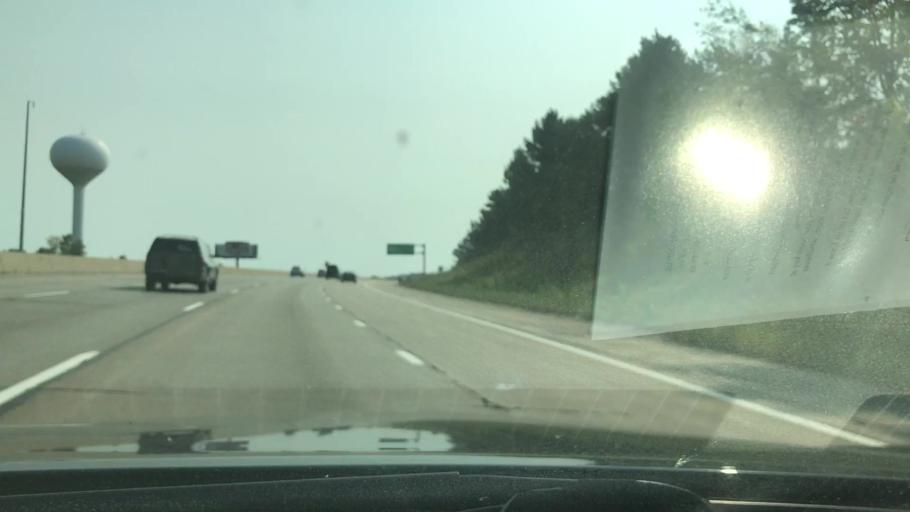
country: US
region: Michigan
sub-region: Livingston County
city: Brighton
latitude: 42.5511
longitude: -83.7974
